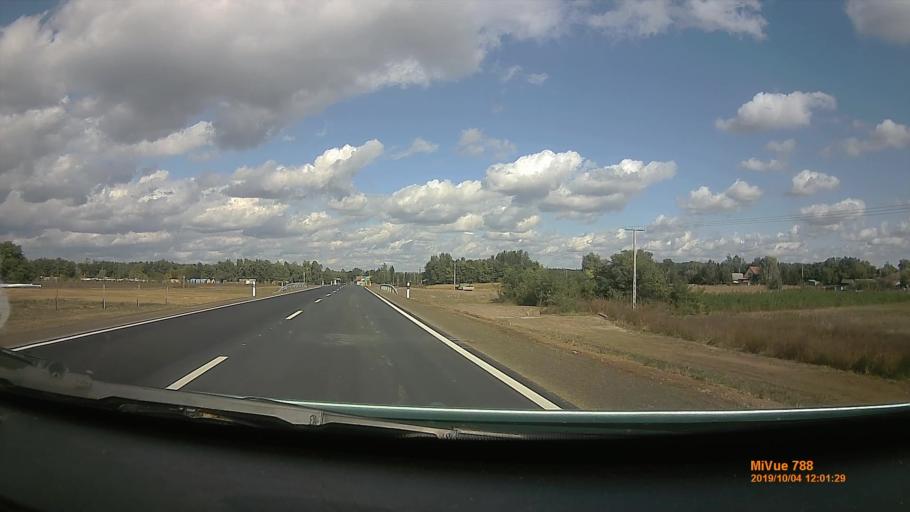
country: HU
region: Szabolcs-Szatmar-Bereg
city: Nyirtelek
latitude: 48.0192
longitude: 21.6792
